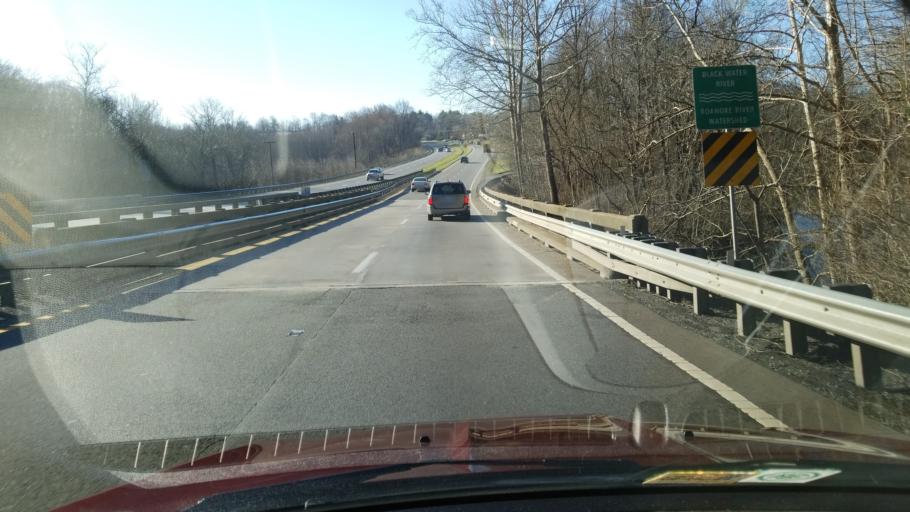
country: US
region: Virginia
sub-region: Franklin County
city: Rocky Mount
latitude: 37.0544
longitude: -79.8825
